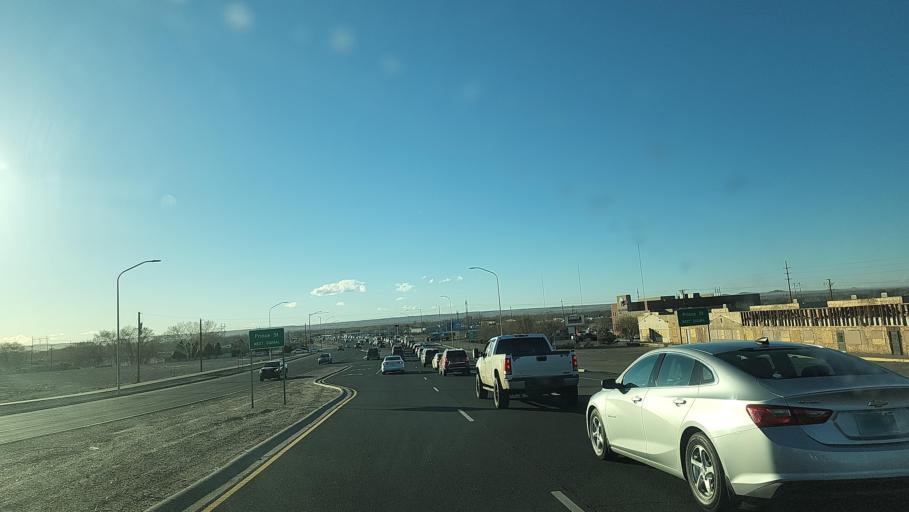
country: US
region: New Mexico
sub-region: Bernalillo County
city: South Valley
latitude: 35.0264
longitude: -106.6504
